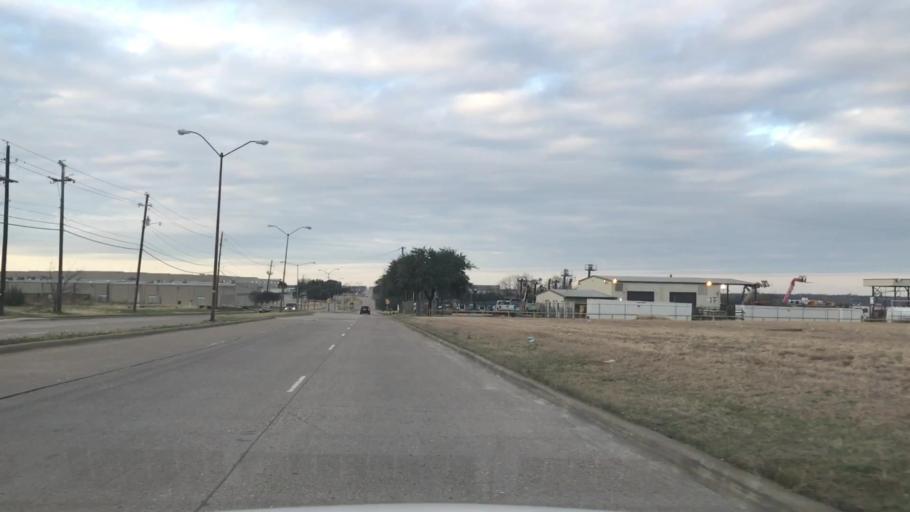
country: US
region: Texas
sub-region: Dallas County
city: Duncanville
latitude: 32.6915
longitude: -96.9085
